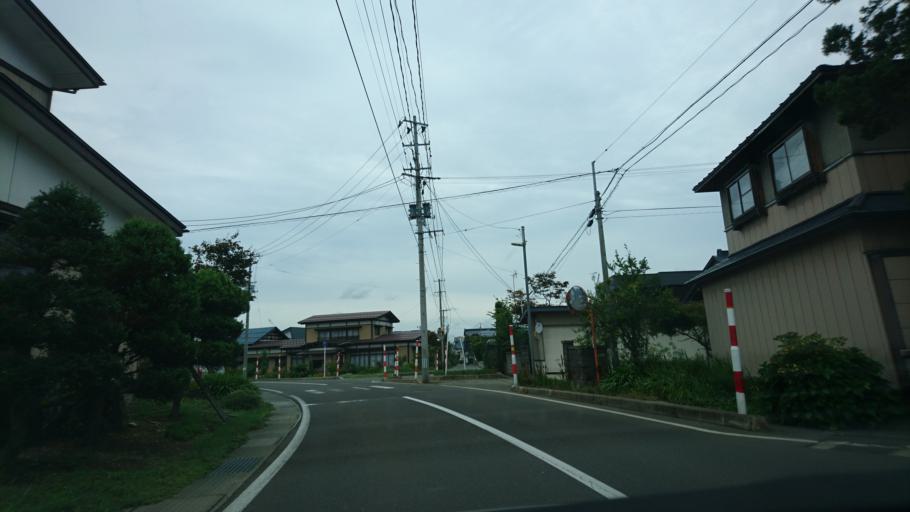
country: JP
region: Akita
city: Yuzawa
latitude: 39.1548
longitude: 140.5678
